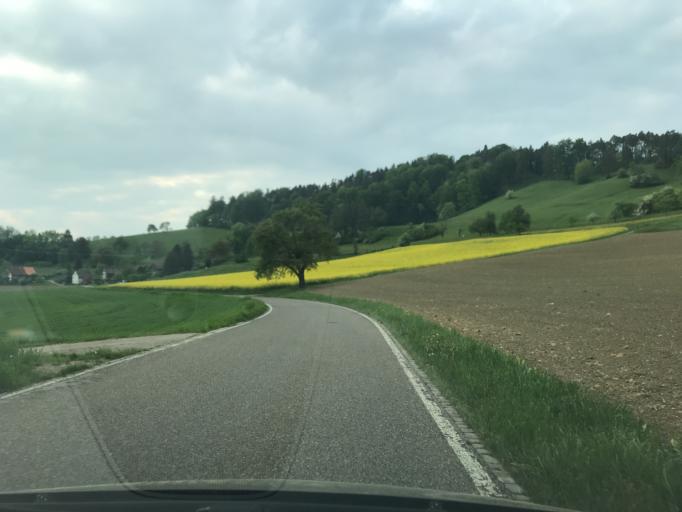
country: CH
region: Zurich
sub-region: Bezirk Winterthur
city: Wuelflingen (Kreis 6) / Oberfeld
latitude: 47.4940
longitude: 8.6861
